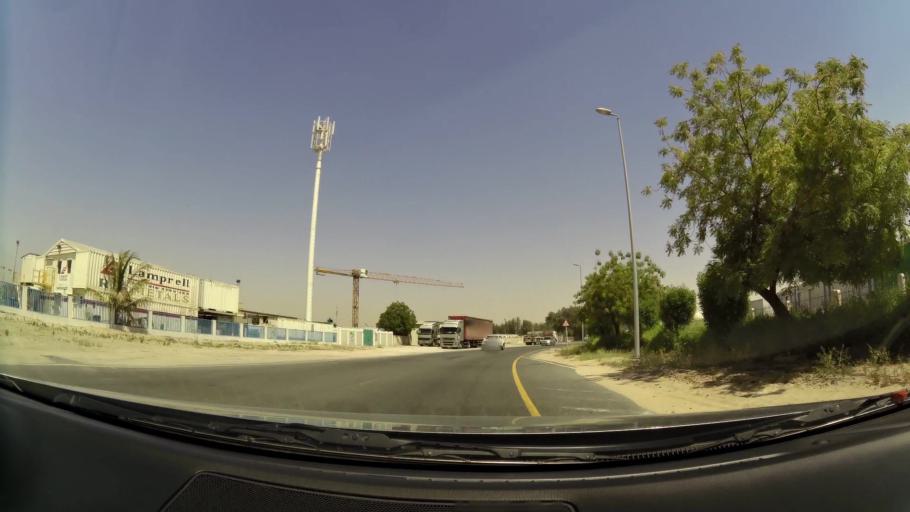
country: AE
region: Dubai
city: Dubai
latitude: 24.9918
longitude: 55.1537
